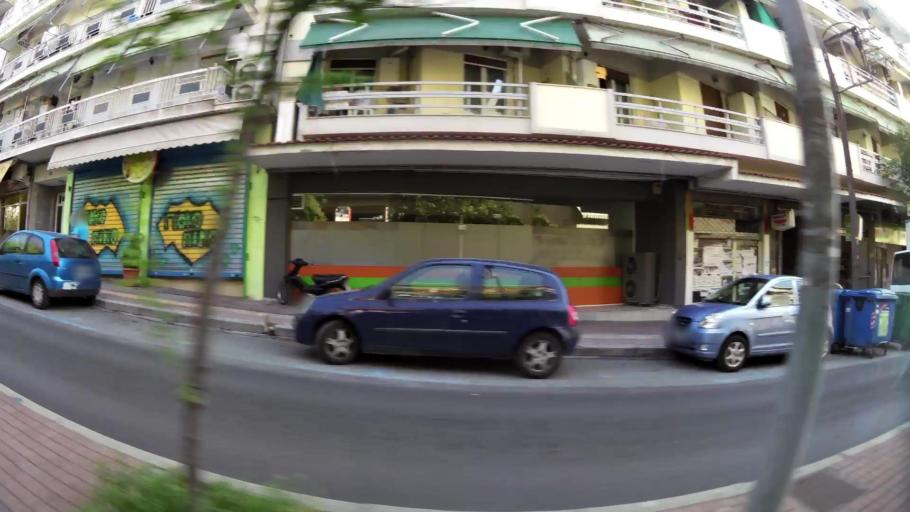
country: GR
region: Central Macedonia
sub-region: Nomos Thessalonikis
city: Agios Pavlos
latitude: 40.6387
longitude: 22.9527
